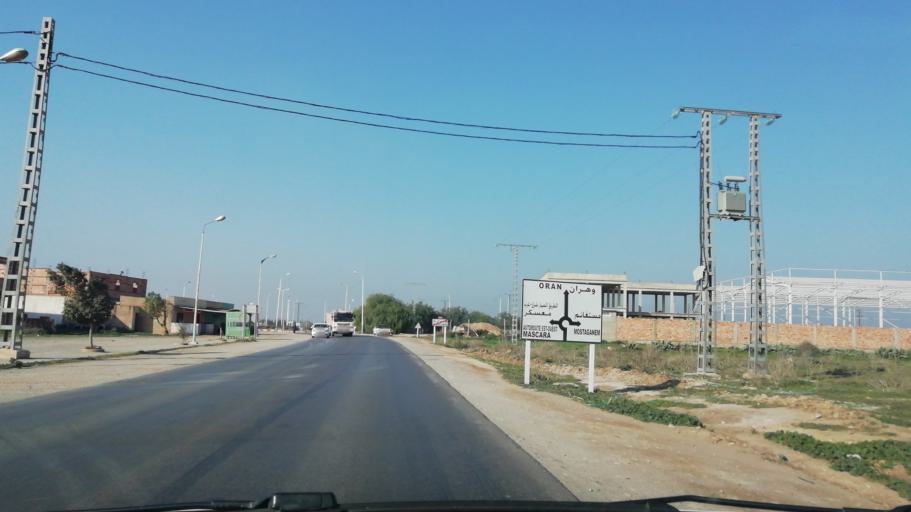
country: DZ
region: Mostaganem
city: Mostaganem
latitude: 35.7554
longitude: 0.0522
